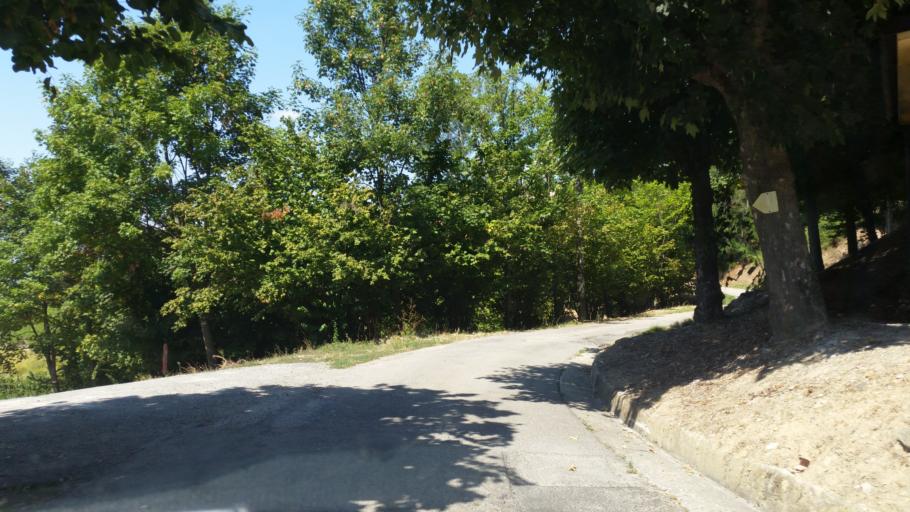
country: IT
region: Piedmont
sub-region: Provincia di Cuneo
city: Mango
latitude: 44.6875
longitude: 8.1563
